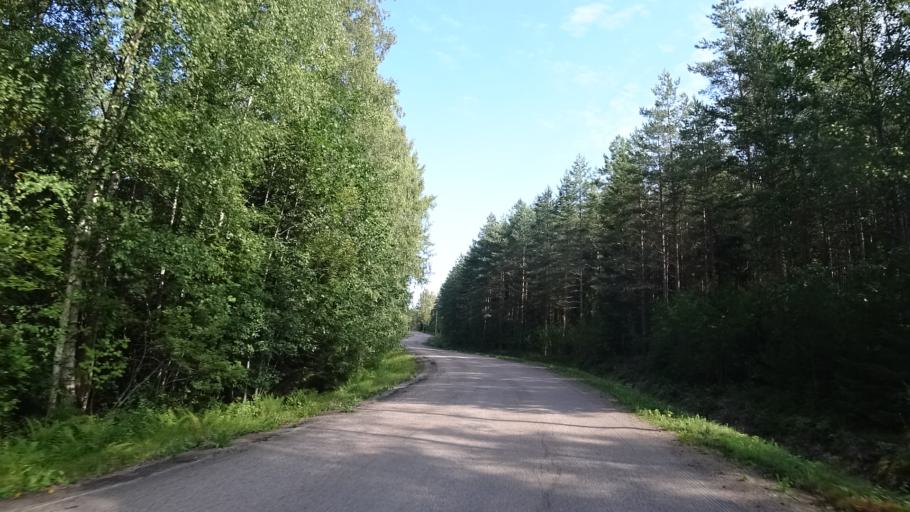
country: FI
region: Kymenlaakso
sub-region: Kotka-Hamina
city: Virojoki
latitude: 60.5903
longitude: 27.7627
